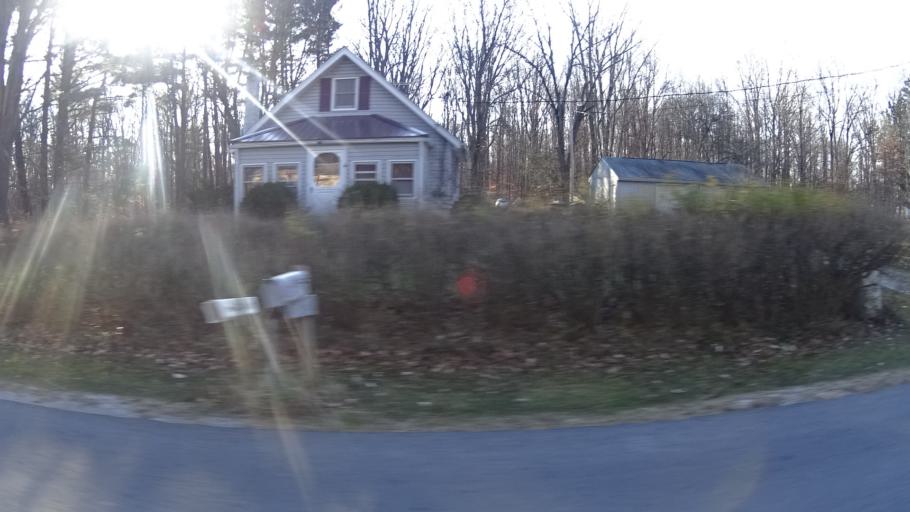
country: US
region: Ohio
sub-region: Lorain County
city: Oberlin
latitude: 41.2511
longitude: -82.1999
